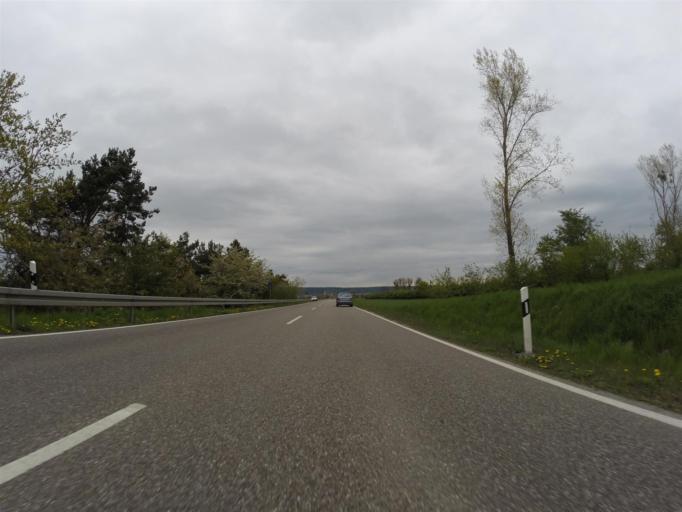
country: DE
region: Saxony-Anhalt
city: Naumburg
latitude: 51.1361
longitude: 11.7931
